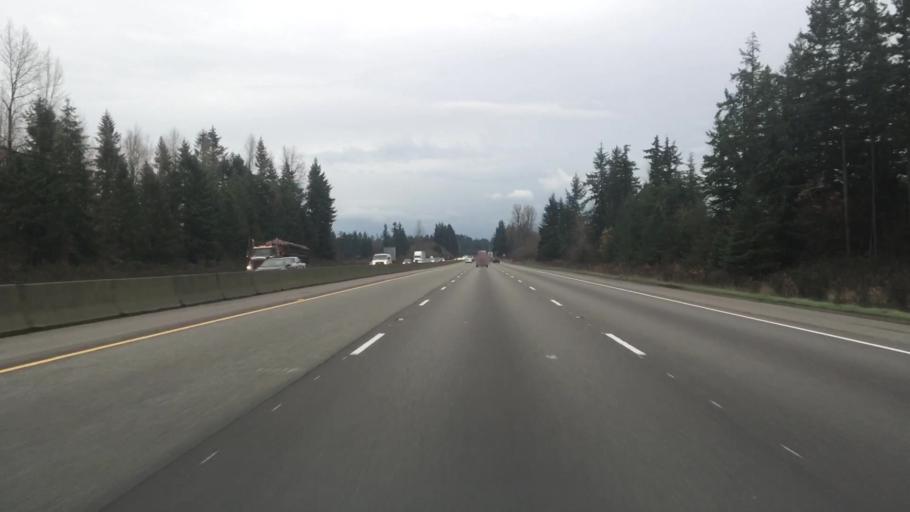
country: US
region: Washington
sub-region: Thurston County
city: Tumwater
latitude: 46.9338
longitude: -122.9432
